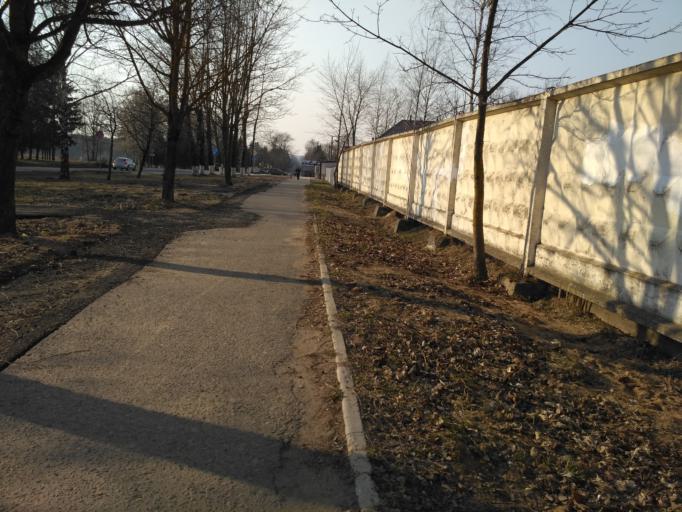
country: BY
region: Minsk
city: Zaslawye
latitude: 54.0153
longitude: 27.2566
